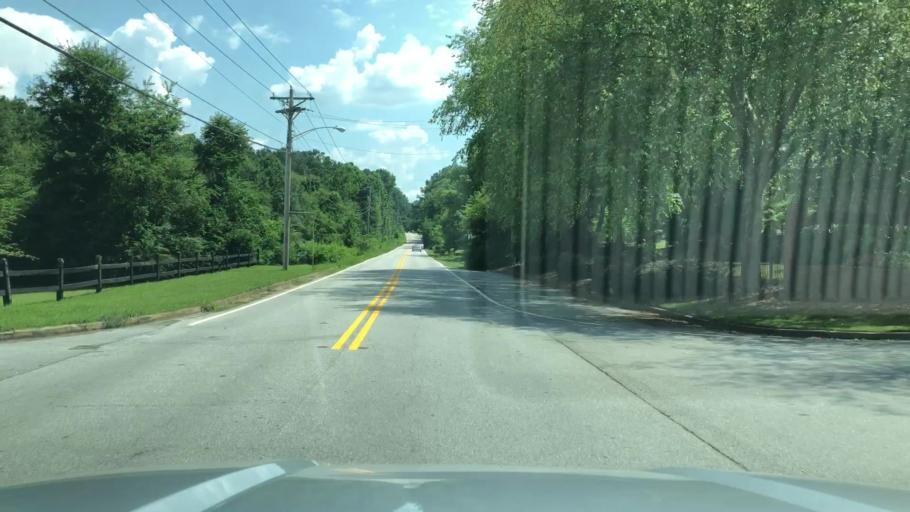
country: US
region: Georgia
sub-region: Paulding County
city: Hiram
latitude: 33.9553
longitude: -84.7260
